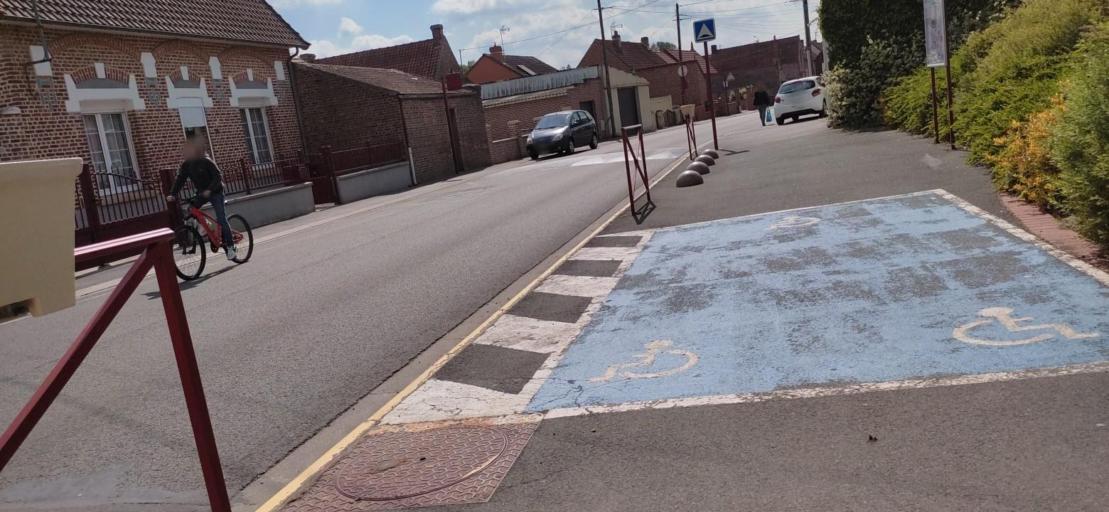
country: FR
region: Nord-Pas-de-Calais
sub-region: Departement du Pas-de-Calais
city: Biache-Saint-Vaast
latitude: 50.3127
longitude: 2.9423
